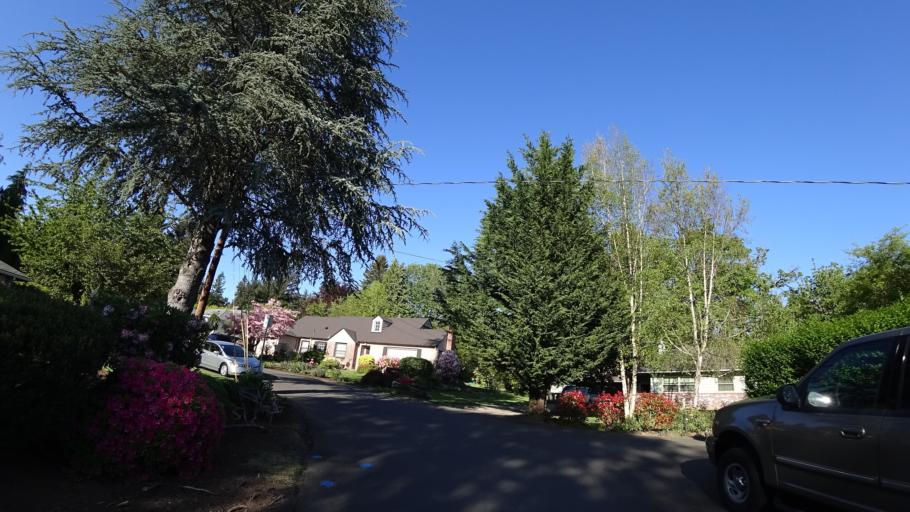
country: US
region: Oregon
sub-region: Washington County
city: West Slope
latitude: 45.4991
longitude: -122.7588
